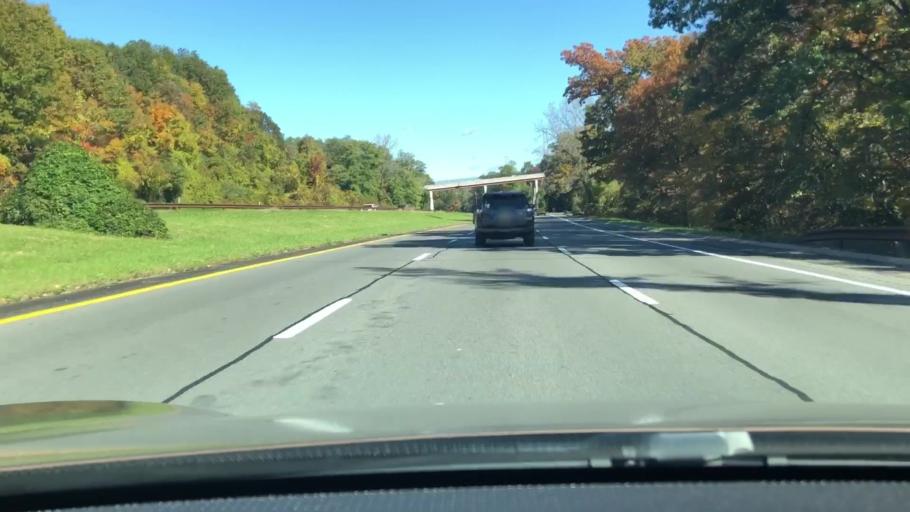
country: US
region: New York
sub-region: Westchester County
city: Ardsley
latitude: 41.0151
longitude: -73.8275
